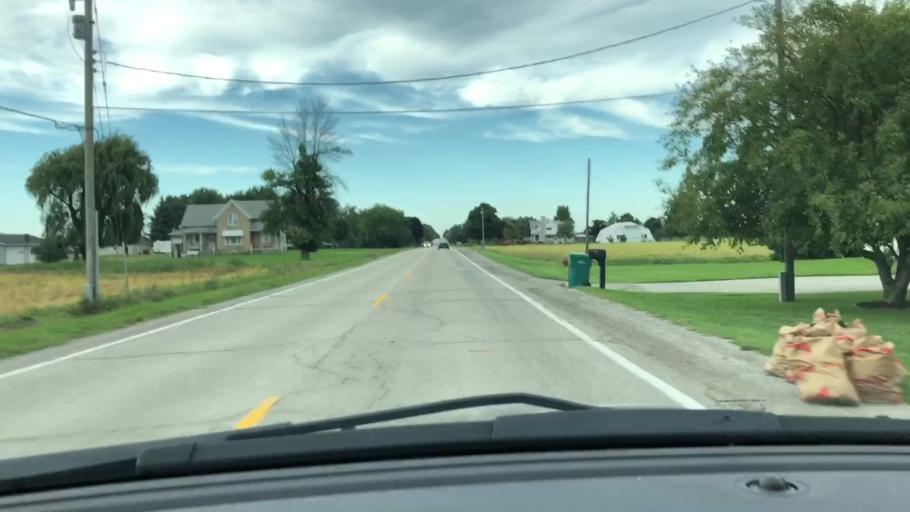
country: US
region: Michigan
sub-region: Bay County
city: Auburn
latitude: 43.5870
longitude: -84.0320
